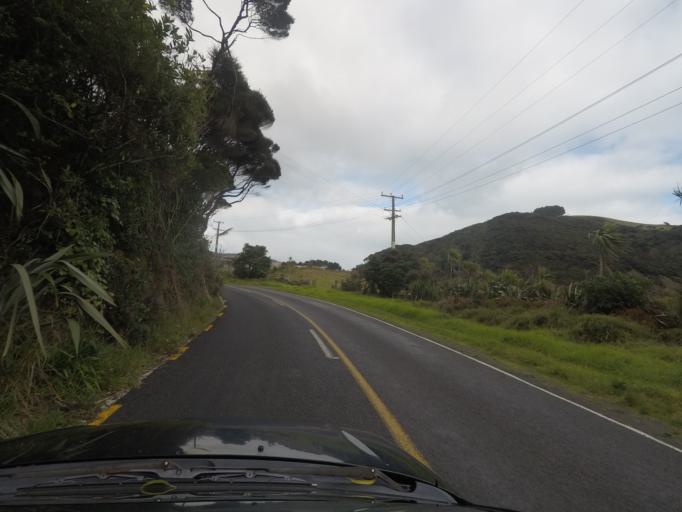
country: NZ
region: Auckland
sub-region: Auckland
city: Muriwai Beach
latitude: -36.8821
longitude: 174.4510
